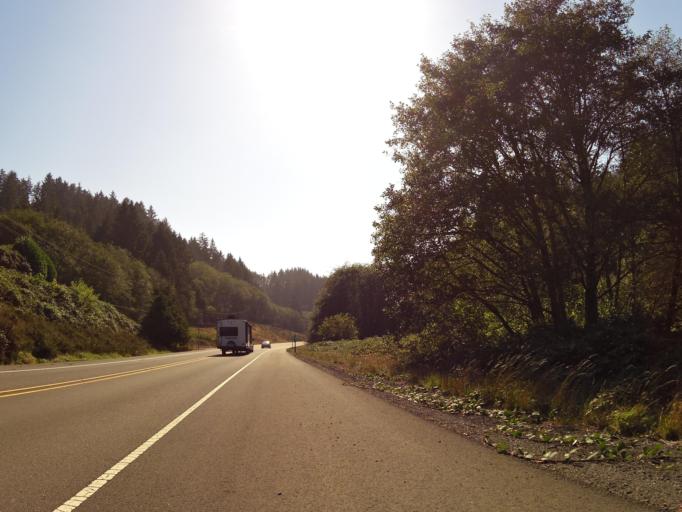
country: US
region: Oregon
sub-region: Tillamook County
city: Pacific City
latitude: 45.1523
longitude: -123.9561
